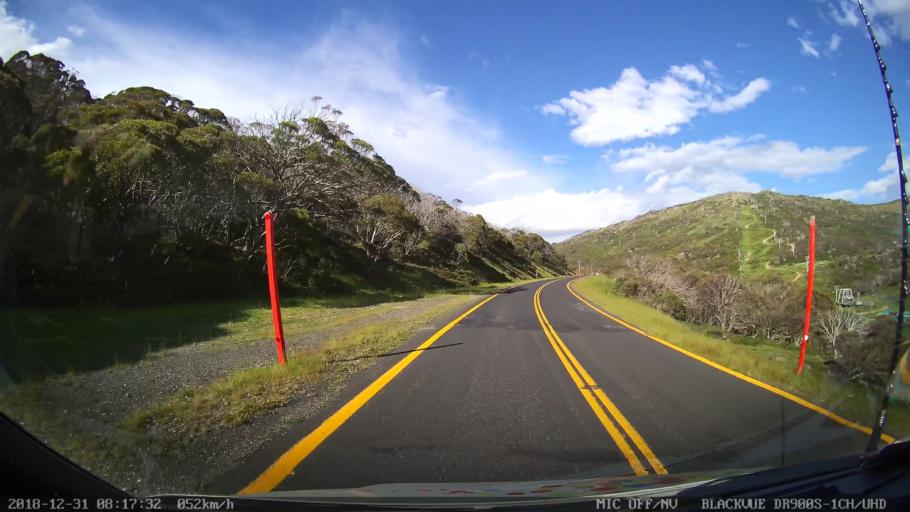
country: AU
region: New South Wales
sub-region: Snowy River
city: Jindabyne
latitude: -36.4109
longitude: 148.4032
